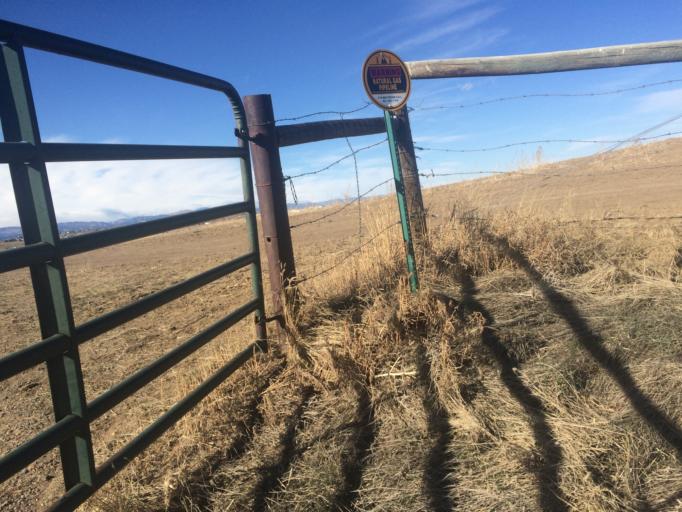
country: US
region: Colorado
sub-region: Broomfield County
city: Broomfield
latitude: 39.9498
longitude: -105.1046
